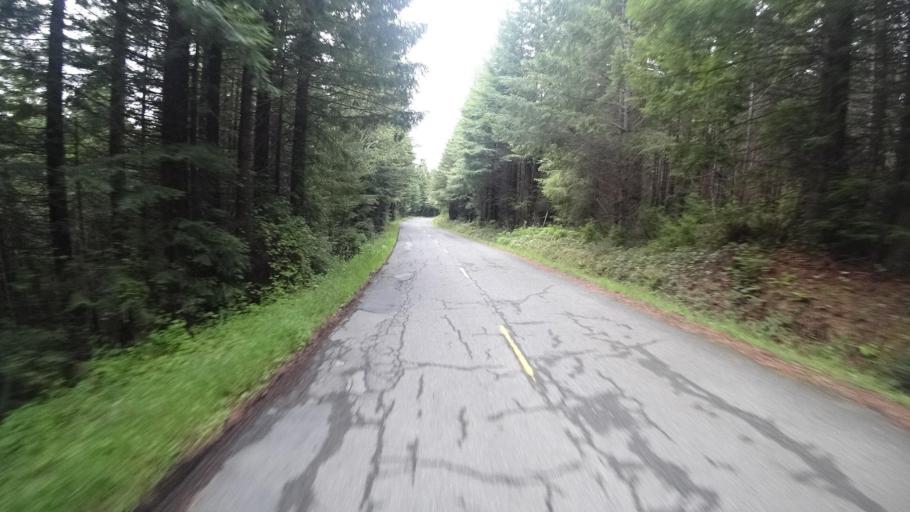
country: US
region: California
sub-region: Humboldt County
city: Blue Lake
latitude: 40.8785
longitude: -123.9703
